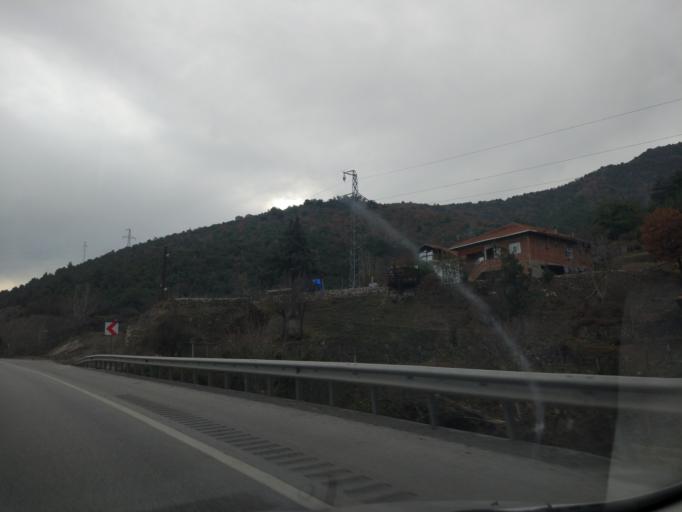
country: TR
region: Karabuk
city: Eskipazar
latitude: 41.0408
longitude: 32.6348
